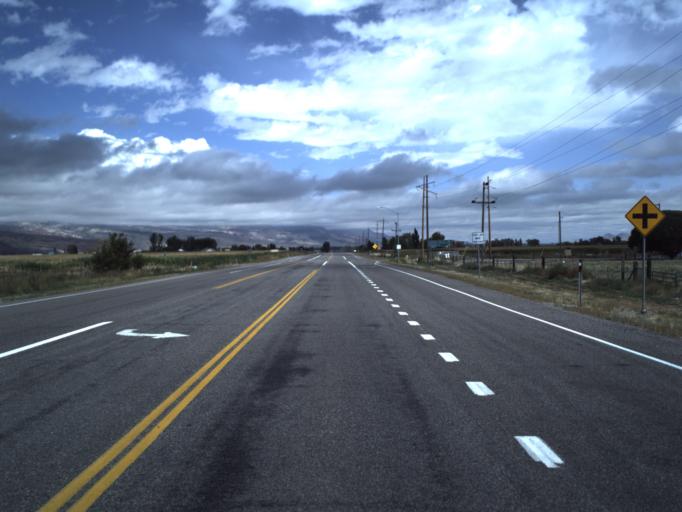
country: US
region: Utah
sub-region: Sevier County
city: Monroe
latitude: 38.7016
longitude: -112.1109
